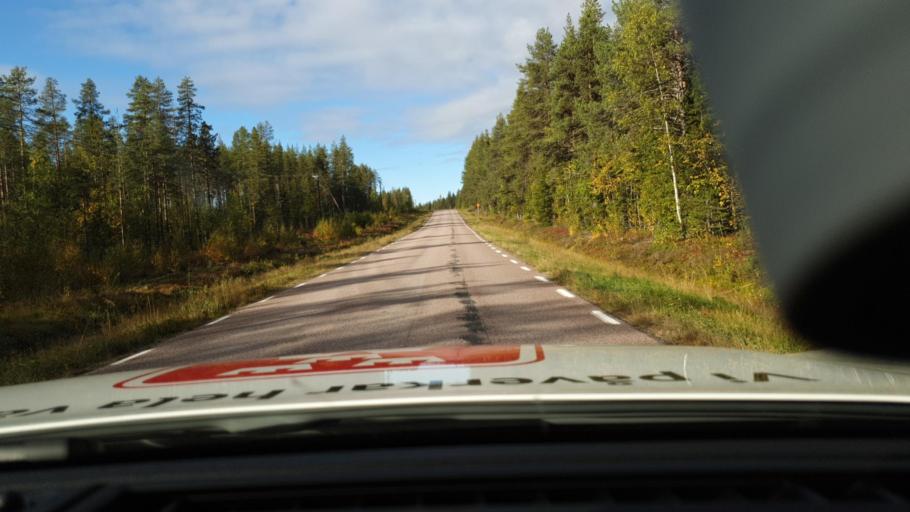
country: SE
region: Norrbotten
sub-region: Pajala Kommun
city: Pajala
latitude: 67.1951
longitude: 23.3375
